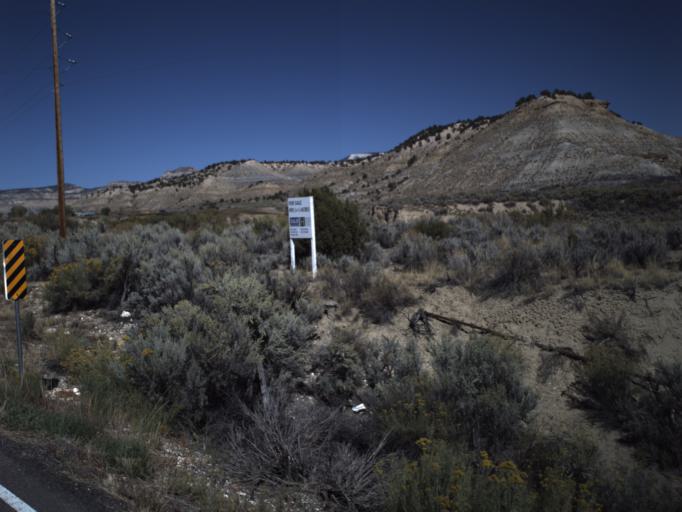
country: US
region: Utah
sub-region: Garfield County
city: Panguitch
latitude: 37.5936
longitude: -112.0622
